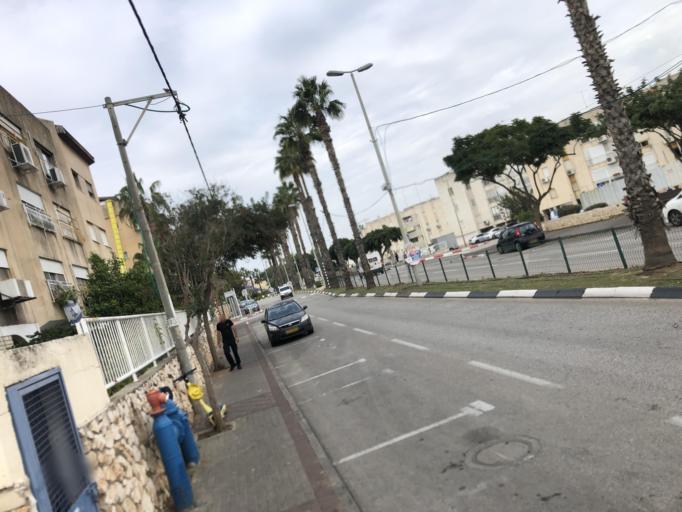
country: IL
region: Northern District
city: `Akko
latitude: 32.9309
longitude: 35.0923
